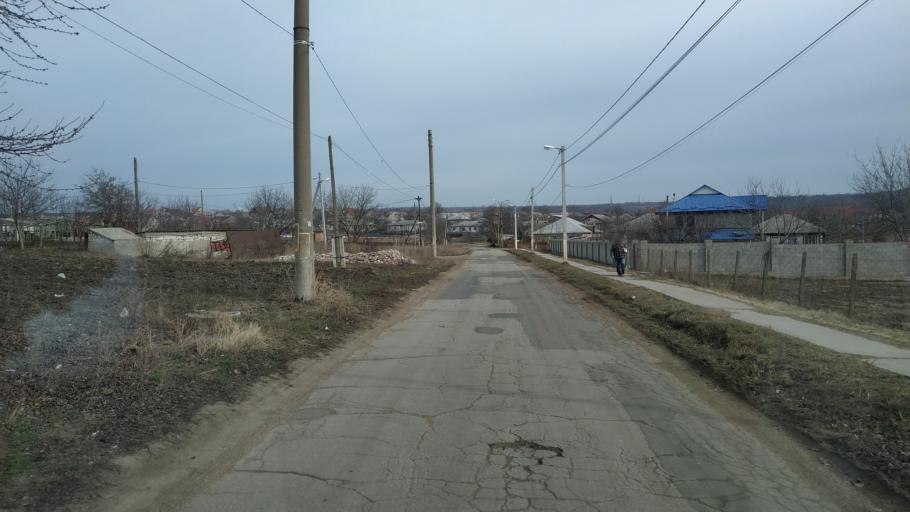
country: MD
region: Chisinau
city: Vatra
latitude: 47.0931
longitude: 28.7607
